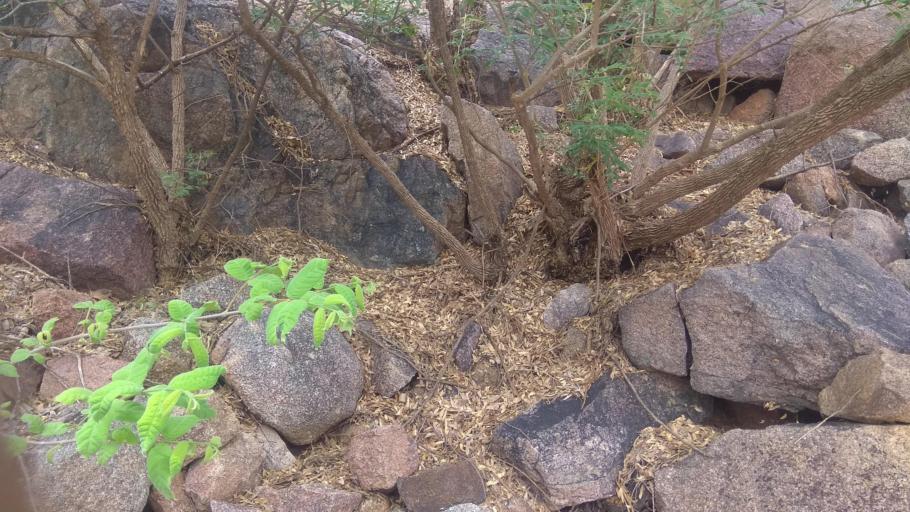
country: IN
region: Telangana
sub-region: Mahbubnagar
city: Farrukhnagar
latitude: 16.8937
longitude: 78.4893
